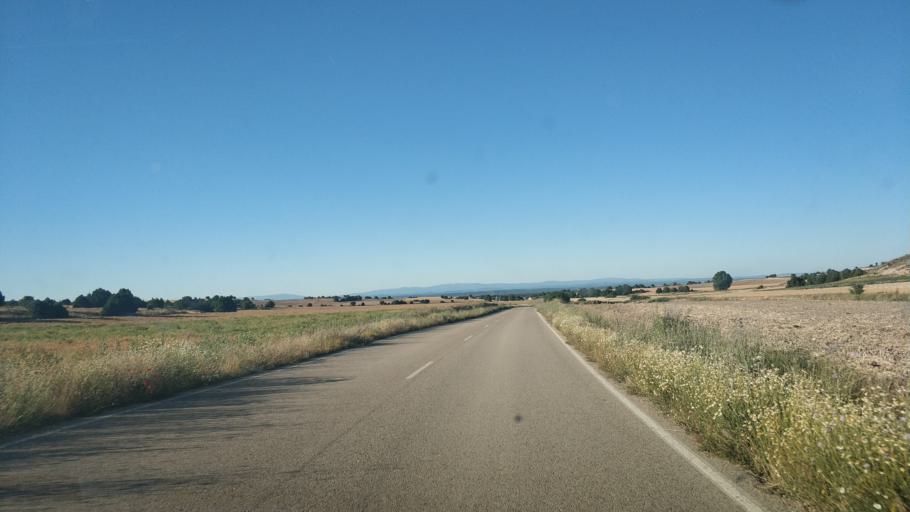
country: ES
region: Castille and Leon
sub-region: Provincia de Soria
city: San Esteban de Gormaz
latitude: 41.4790
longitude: -3.2155
